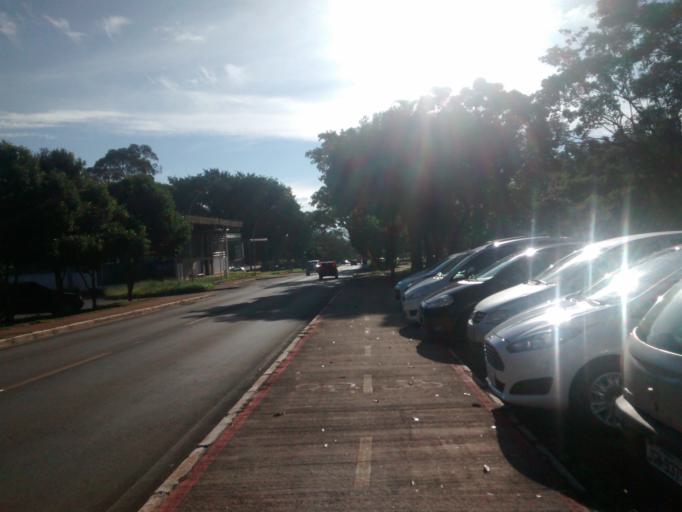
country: BR
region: Federal District
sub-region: Brasilia
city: Brasilia
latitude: -15.7674
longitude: -47.8719
